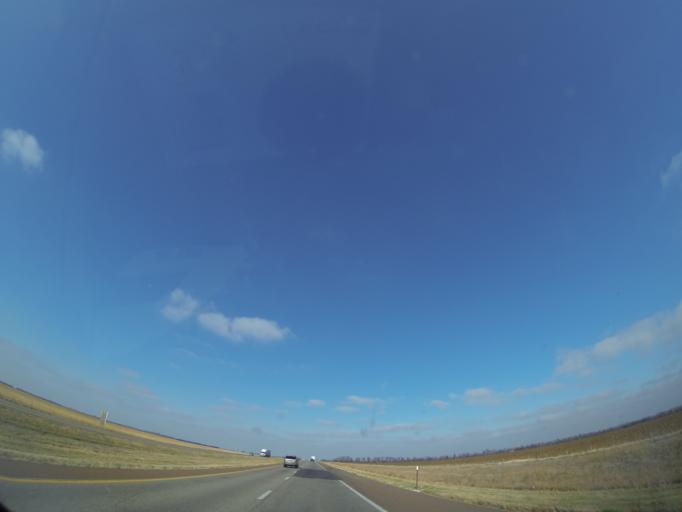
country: US
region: Kansas
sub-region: McPherson County
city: McPherson
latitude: 38.4232
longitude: -97.6206
